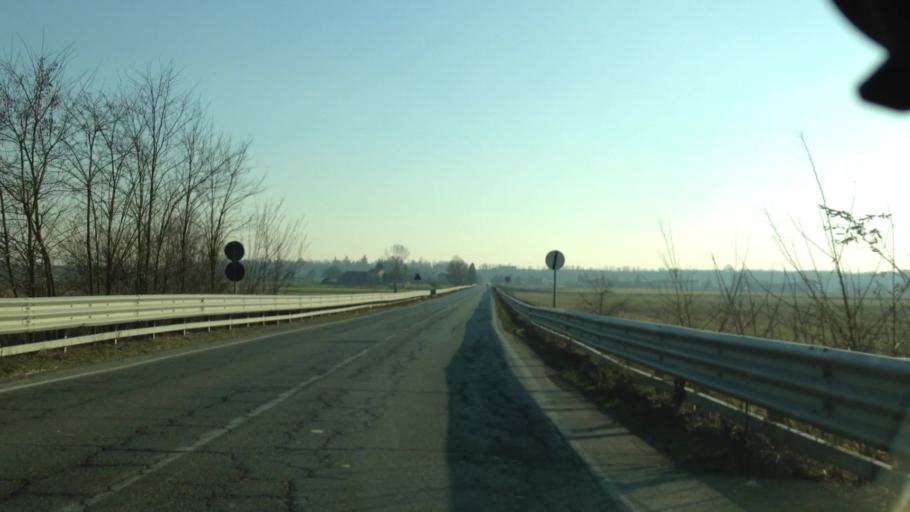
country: IT
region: Piedmont
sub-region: Provincia di Alessandria
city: Felizzano
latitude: 44.8879
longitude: 8.4404
